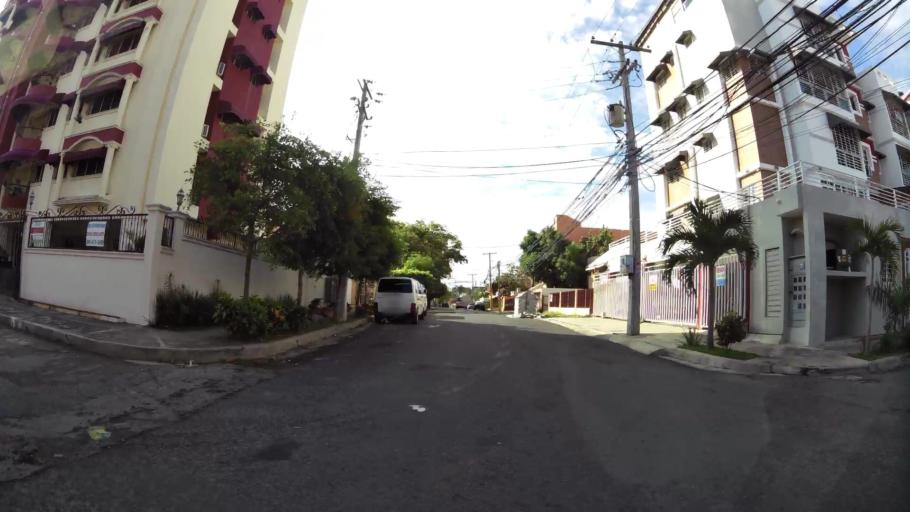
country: DO
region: Santo Domingo
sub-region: Santo Domingo
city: Santo Domingo Este
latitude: 18.4877
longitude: -69.8590
